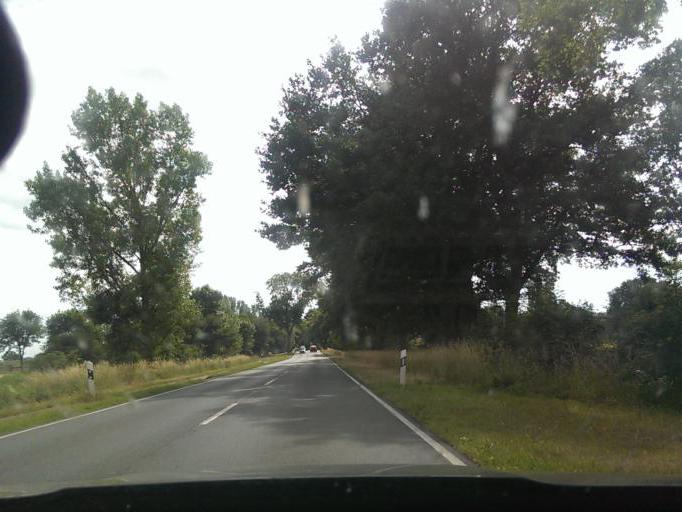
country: DE
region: Lower Saxony
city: Essel
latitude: 52.6940
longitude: 9.6486
